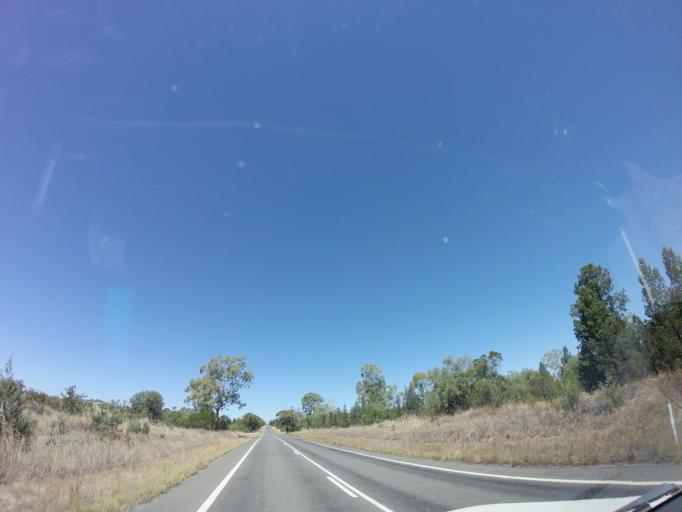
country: AU
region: New South Wales
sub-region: Bogan
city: Nyngan
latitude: -31.5505
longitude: 146.6774
